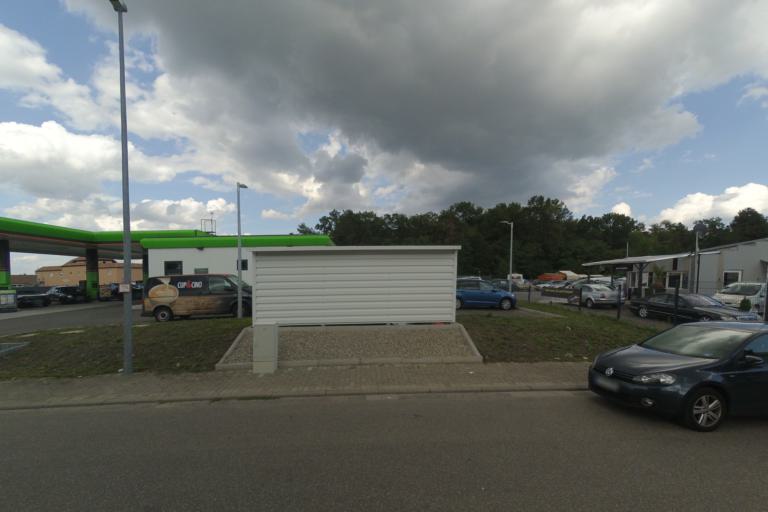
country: DE
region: Rheinland-Pfalz
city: Schifferstadt
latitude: 49.3856
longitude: 8.3950
